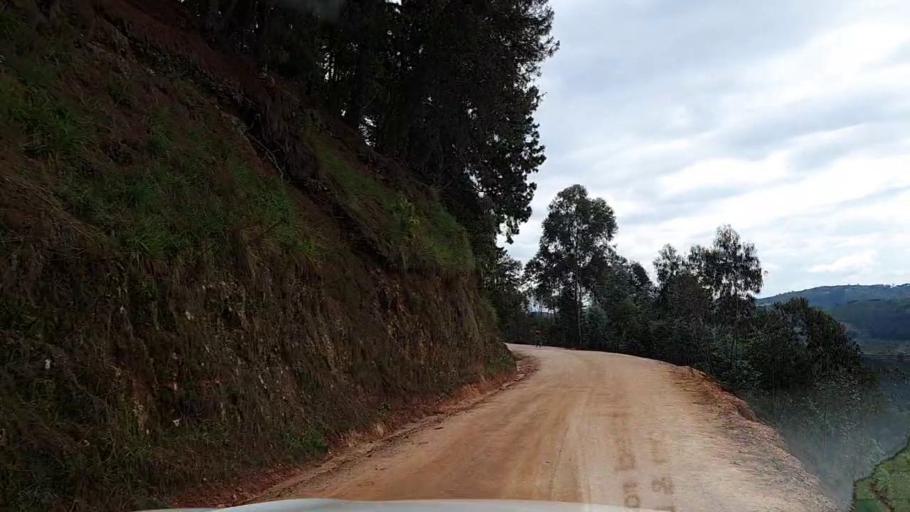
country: RW
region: Southern Province
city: Nzega
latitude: -2.4077
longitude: 29.4539
